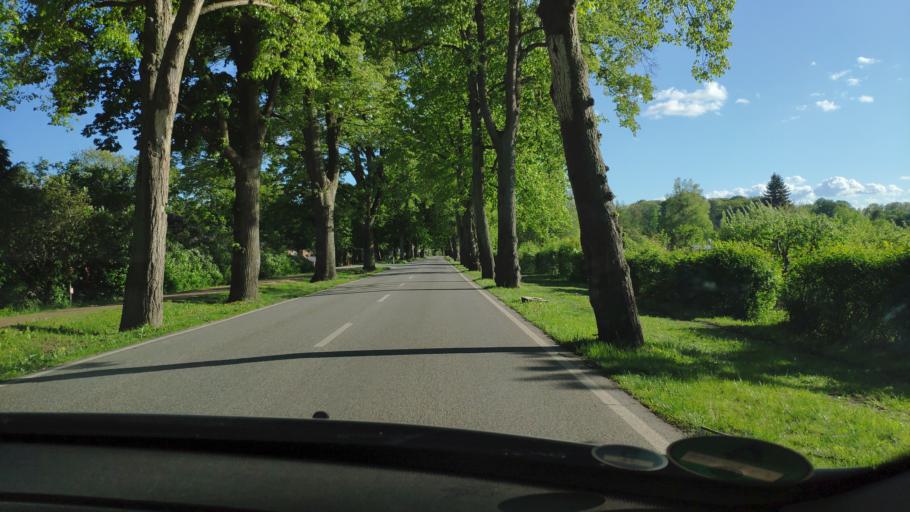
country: DE
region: Mecklenburg-Vorpommern
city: Neustrelitz
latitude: 53.3594
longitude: 13.0516
